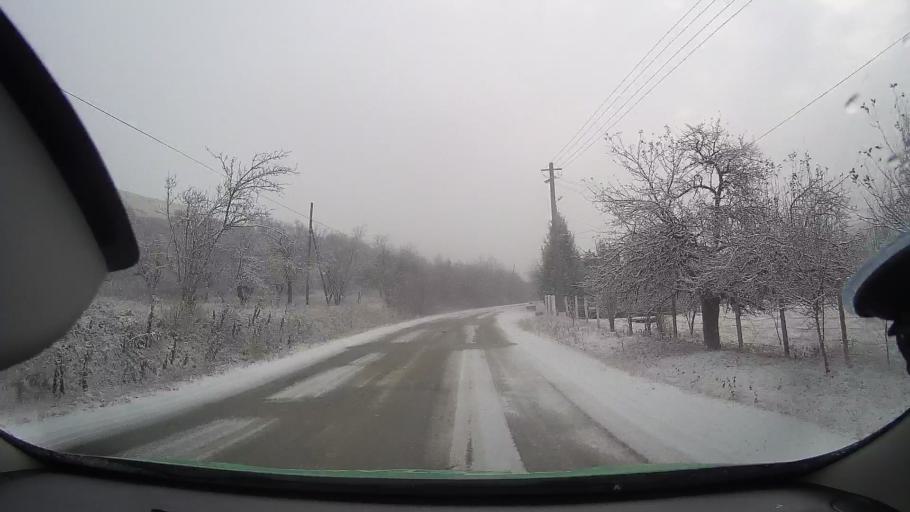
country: RO
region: Alba
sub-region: Municipiul Aiud
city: Aiudul de Sus
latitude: 46.3377
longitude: 23.6701
